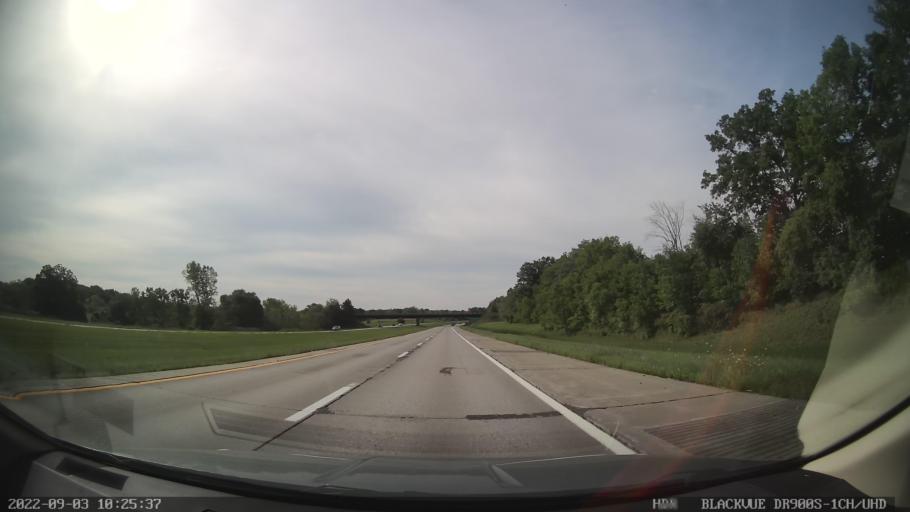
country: US
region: New York
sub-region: Livingston County
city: Avon
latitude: 42.8481
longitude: -77.7302
